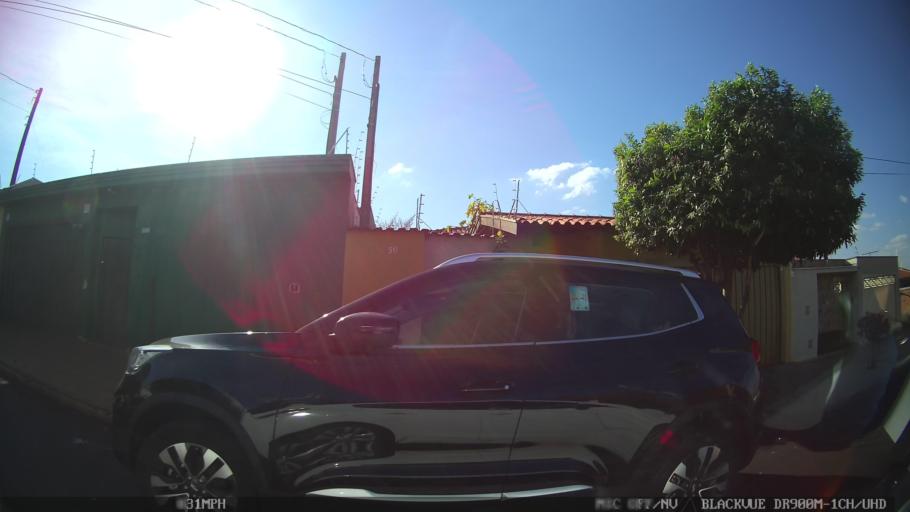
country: BR
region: Sao Paulo
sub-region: Ribeirao Preto
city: Ribeirao Preto
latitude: -21.1751
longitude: -47.7634
